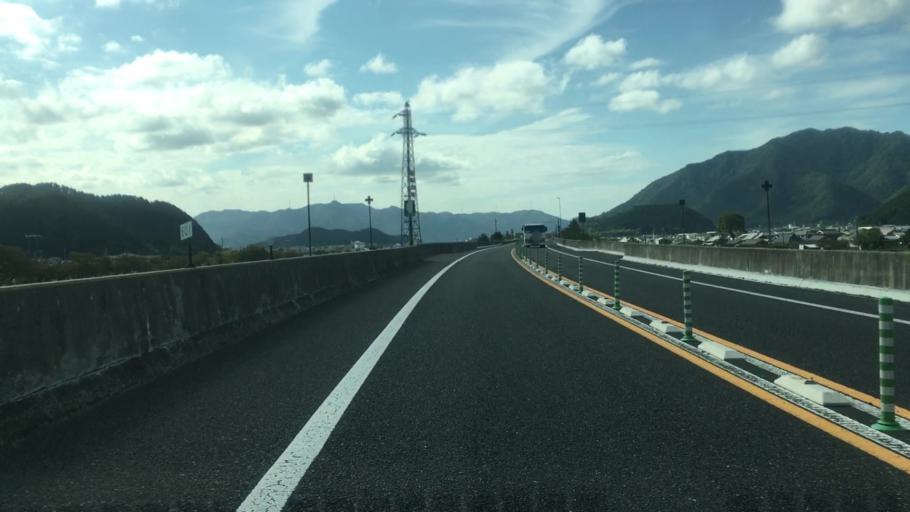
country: JP
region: Kyoto
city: Fukuchiyama
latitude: 35.1931
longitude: 135.0426
